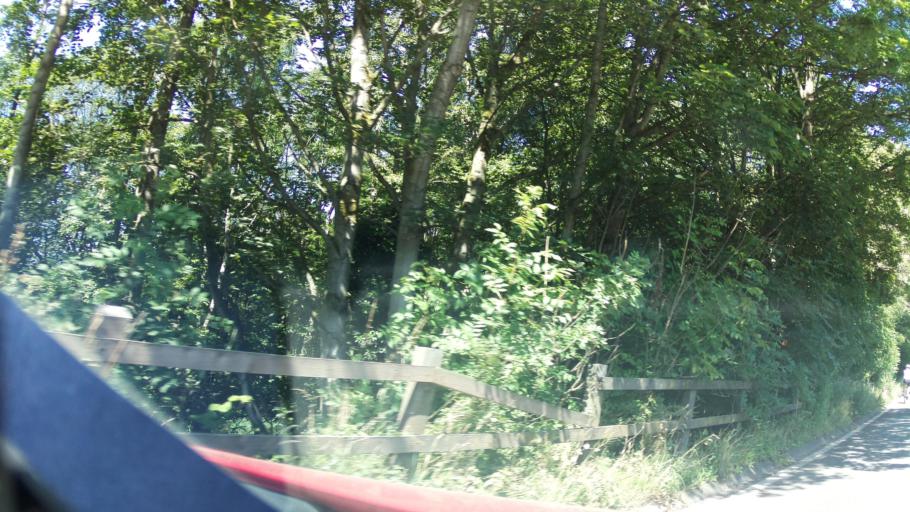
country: GB
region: England
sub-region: Derbyshire
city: Bakewell
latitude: 53.1873
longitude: -1.6119
